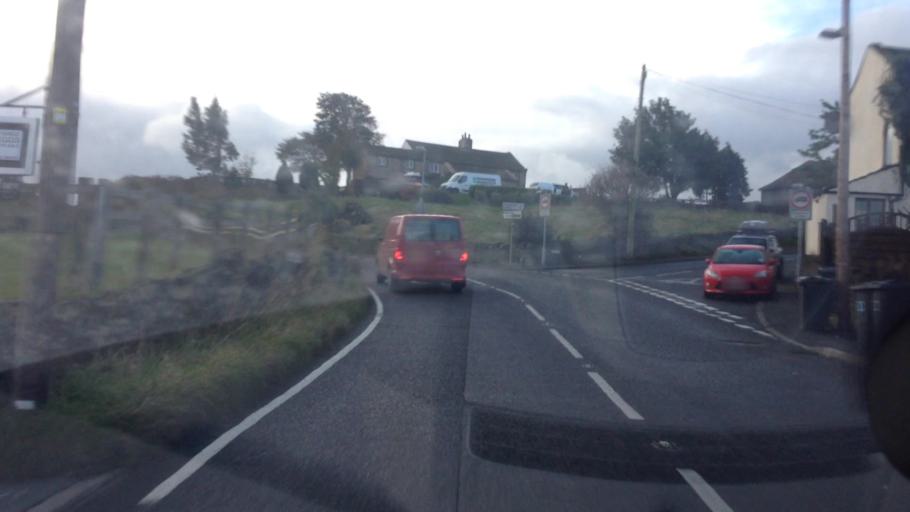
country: GB
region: England
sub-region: Kirklees
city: Mirfield
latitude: 53.6677
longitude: -1.7327
